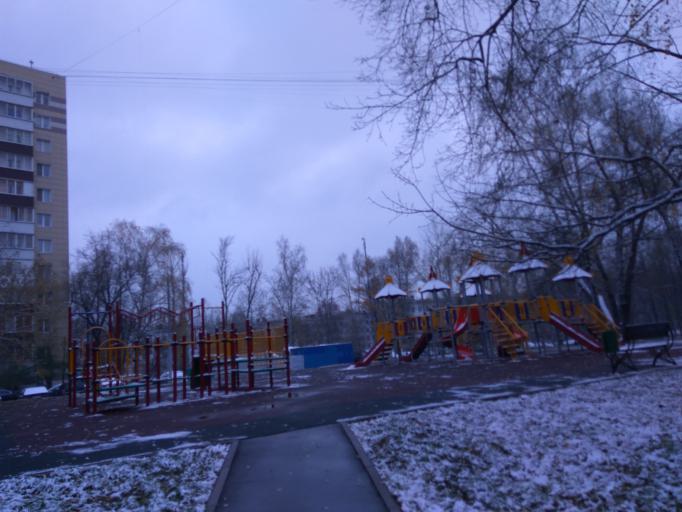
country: RU
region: Moscow
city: Orekhovo-Borisovo Severnoye
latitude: 55.6323
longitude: 37.6700
